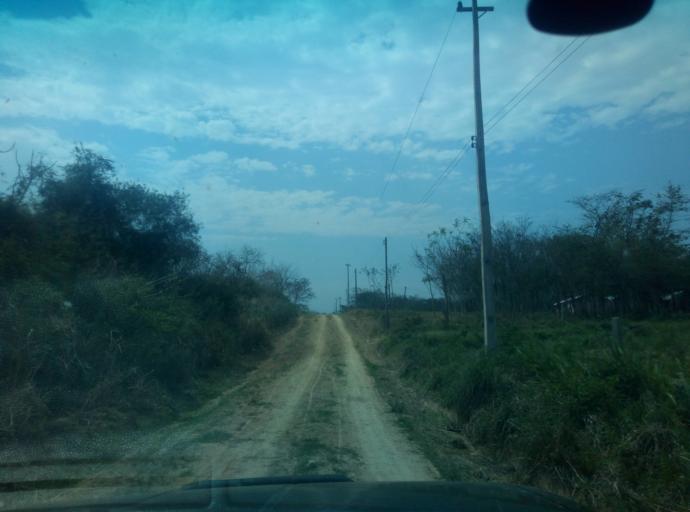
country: PY
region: Caaguazu
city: Doctor Cecilio Baez
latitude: -25.1382
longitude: -56.1619
